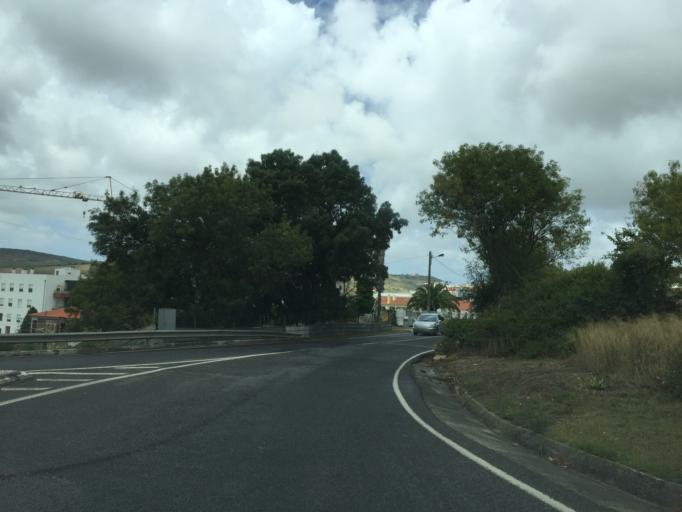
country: PT
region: Lisbon
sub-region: Torres Vedras
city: Torres Vedras
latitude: 39.0755
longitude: -9.2516
